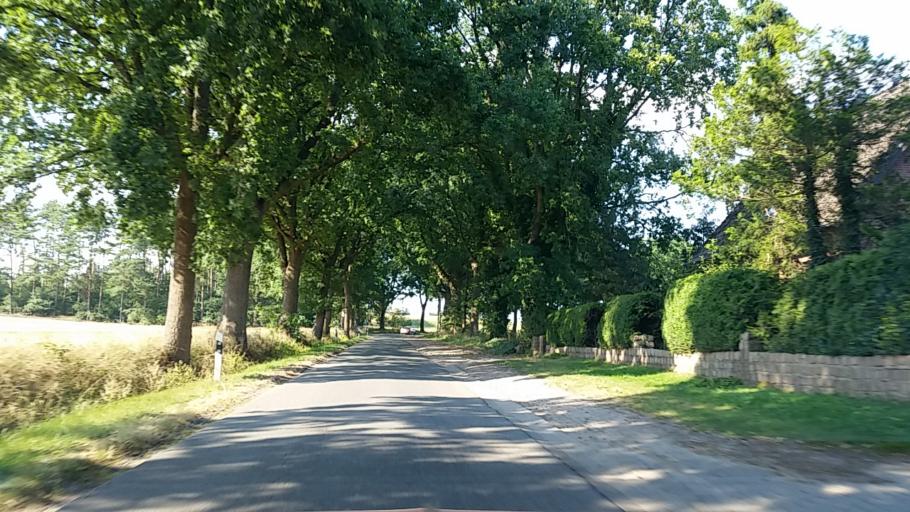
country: DE
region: Lower Saxony
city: Buchholz in der Nordheide
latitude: 53.2771
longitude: 9.8972
